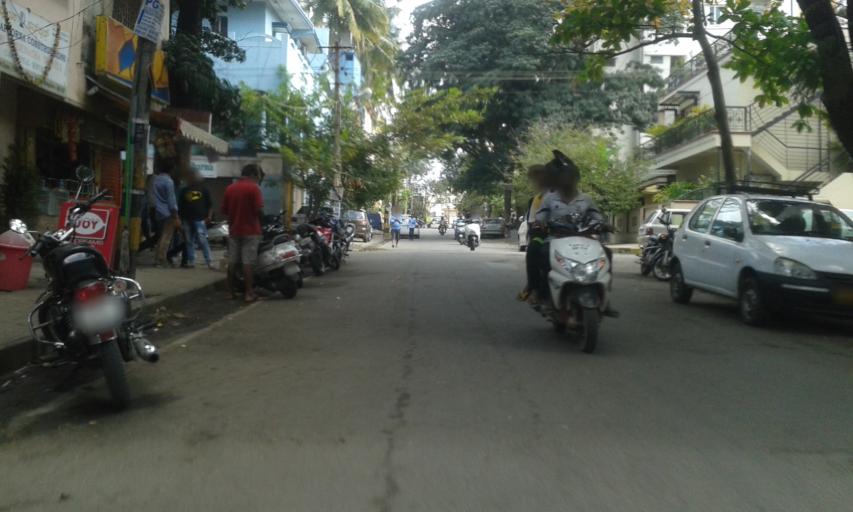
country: IN
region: Karnataka
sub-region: Bangalore Urban
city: Bangalore
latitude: 12.9467
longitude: 77.5965
